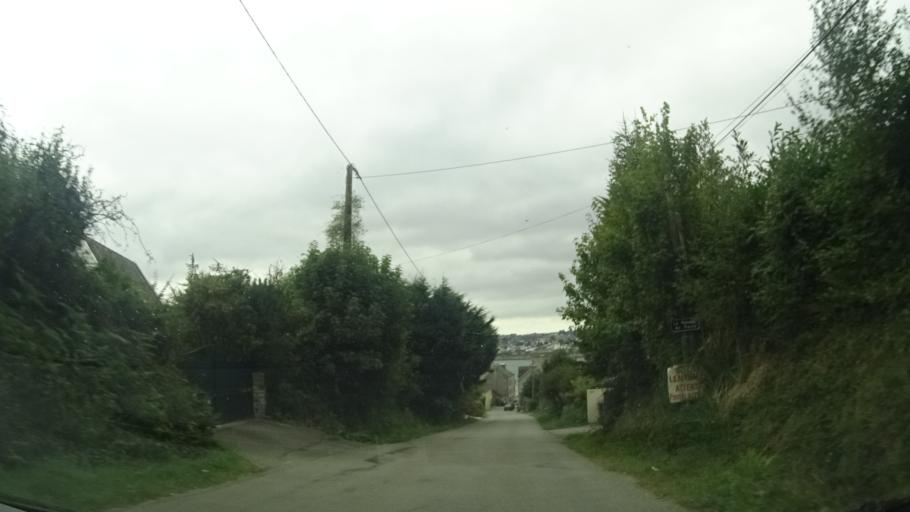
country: FR
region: Brittany
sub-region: Departement du Finistere
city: Le Relecq-Kerhuon
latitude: 48.3900
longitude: -4.3802
